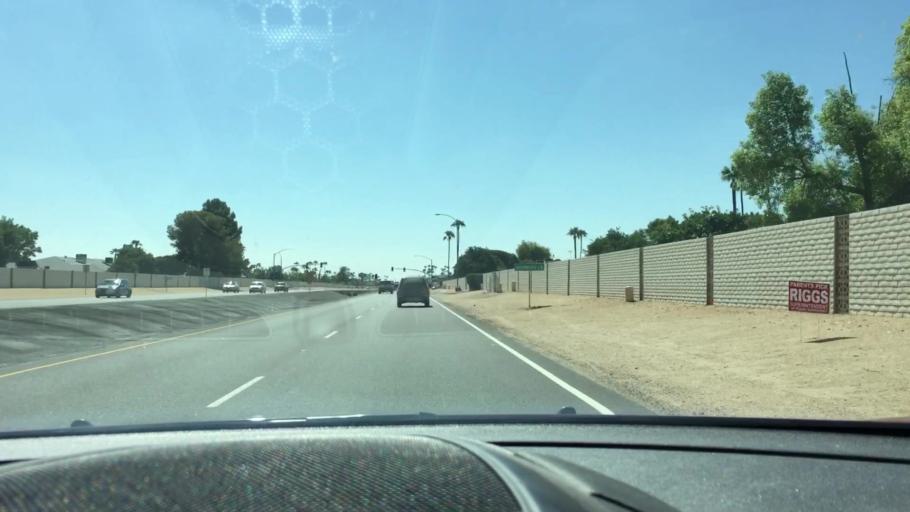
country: US
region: Arizona
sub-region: Maricopa County
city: Sun City
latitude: 33.6486
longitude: -112.2777
